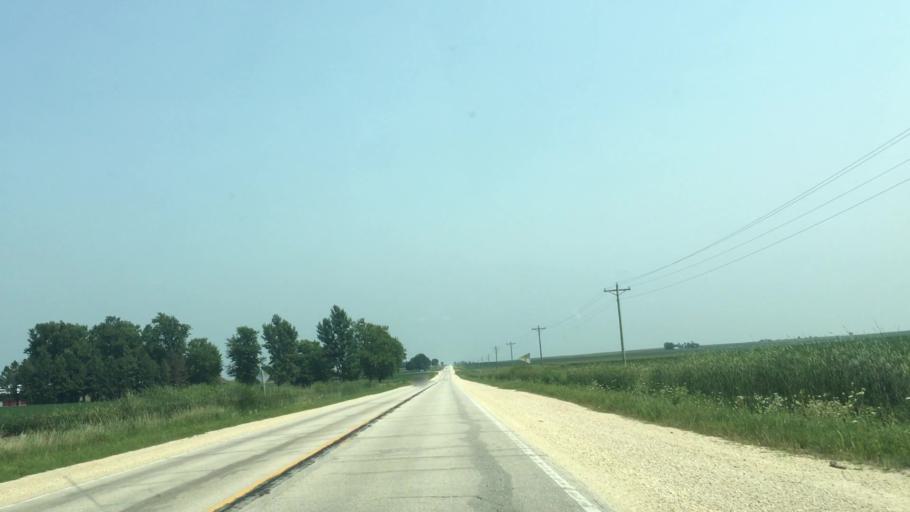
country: US
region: Iowa
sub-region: Fayette County
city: Oelwein
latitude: 42.6874
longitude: -91.8158
